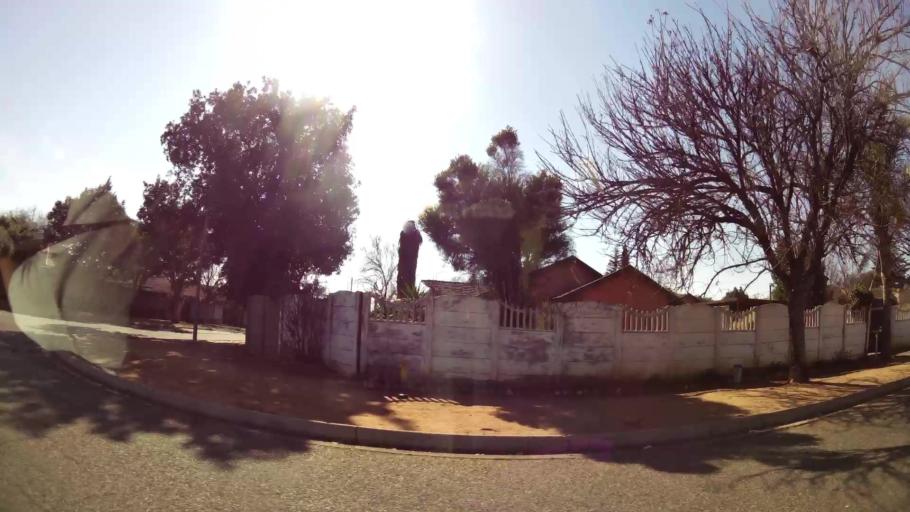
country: ZA
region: Gauteng
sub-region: Ekurhuleni Metropolitan Municipality
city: Tembisa
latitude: -26.0439
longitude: 28.2058
